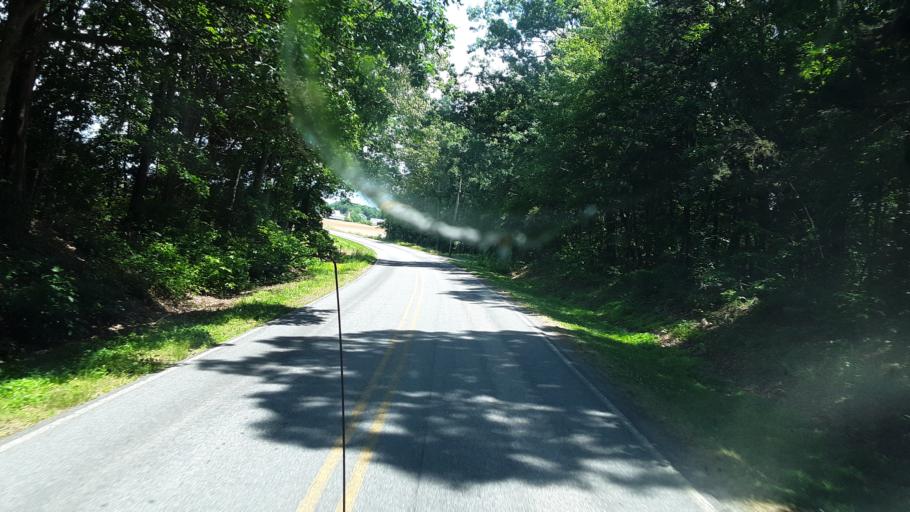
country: US
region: North Carolina
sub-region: Yadkin County
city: Jonesville
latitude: 36.0775
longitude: -80.8567
